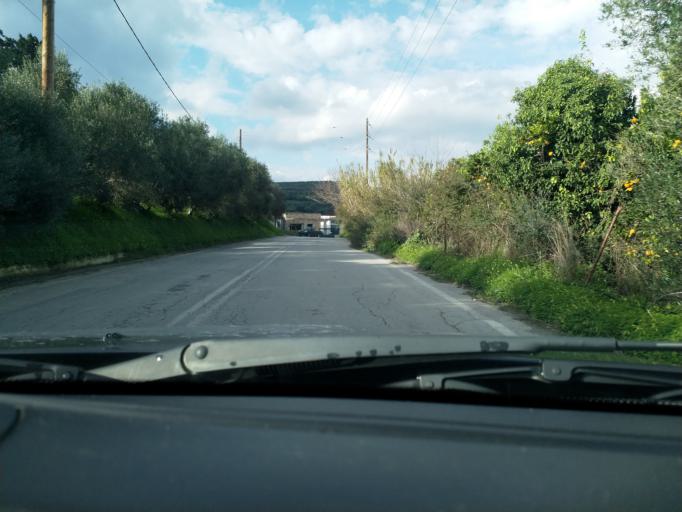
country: GR
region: Crete
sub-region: Nomos Chanias
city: Gerani
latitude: 35.5019
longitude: 23.8971
